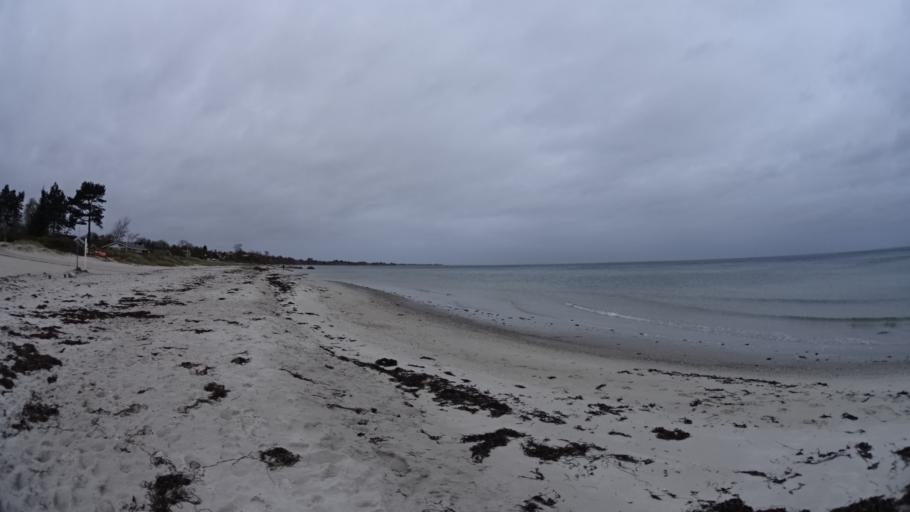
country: DK
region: Central Jutland
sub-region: Arhus Kommune
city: Malling
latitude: 55.9807
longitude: 10.2527
